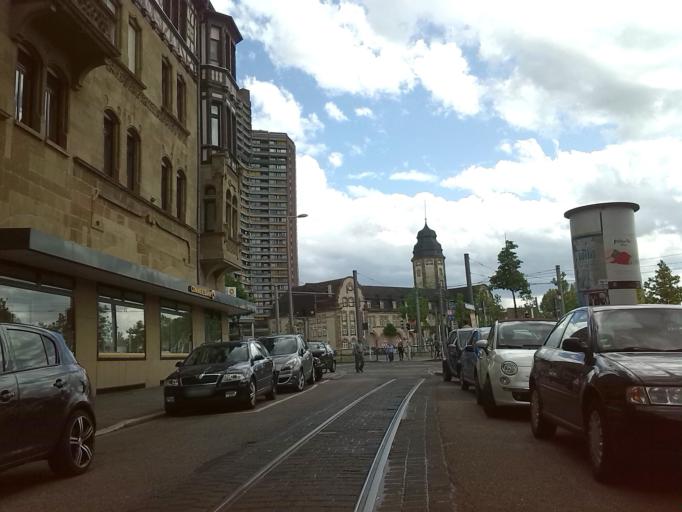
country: DE
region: Baden-Wuerttemberg
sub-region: Karlsruhe Region
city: Mannheim
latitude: 49.4974
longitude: 8.4736
